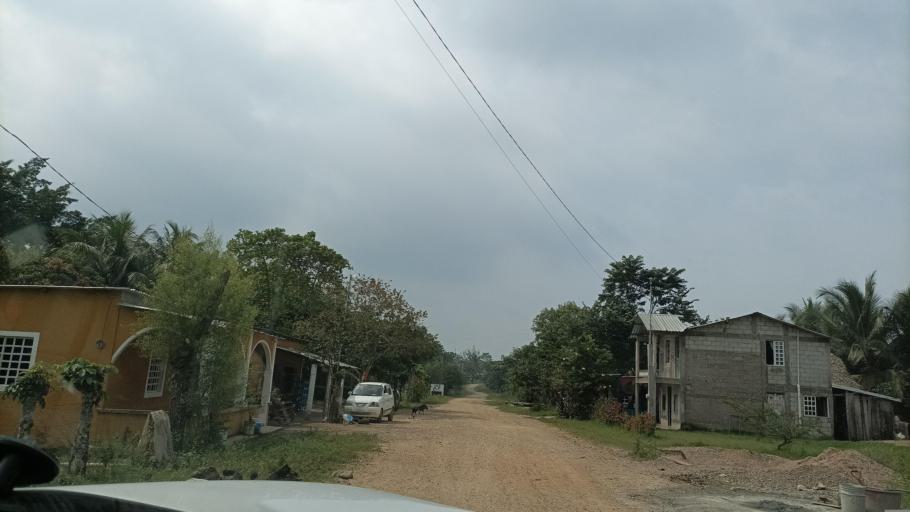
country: MX
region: Veracruz
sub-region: Moloacan
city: Cuichapa
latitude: 17.5787
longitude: -94.2289
